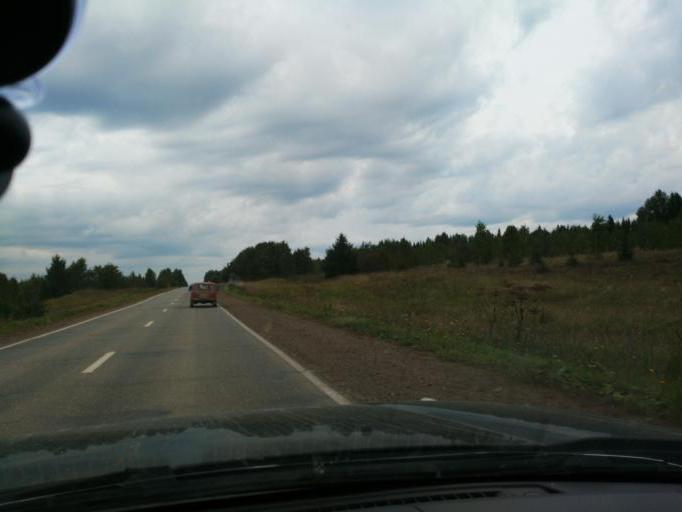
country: RU
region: Perm
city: Chernushka
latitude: 56.7514
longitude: 56.1516
